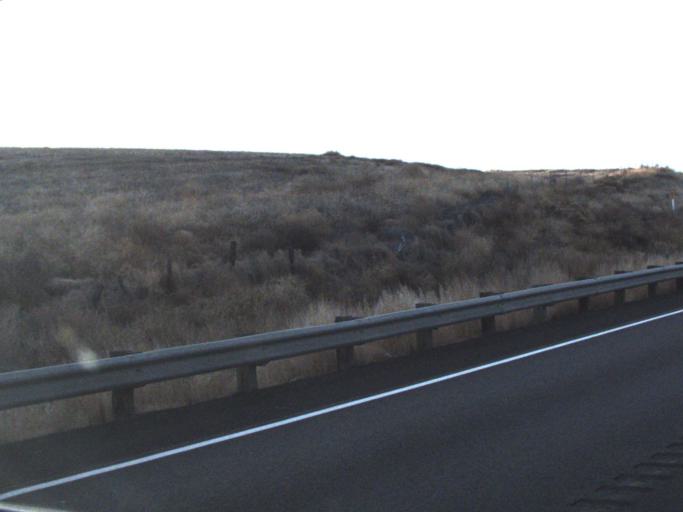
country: US
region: Washington
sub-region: Walla Walla County
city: Garrett
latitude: 46.0516
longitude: -118.7074
